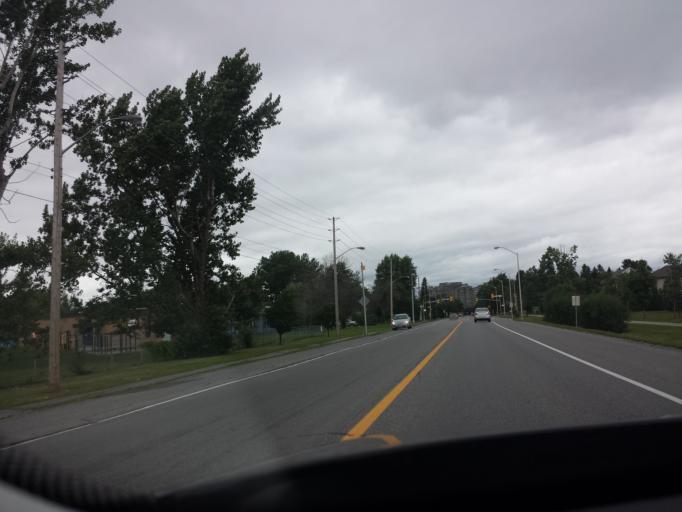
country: CA
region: Ontario
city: Ottawa
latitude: 45.3596
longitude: -75.6998
